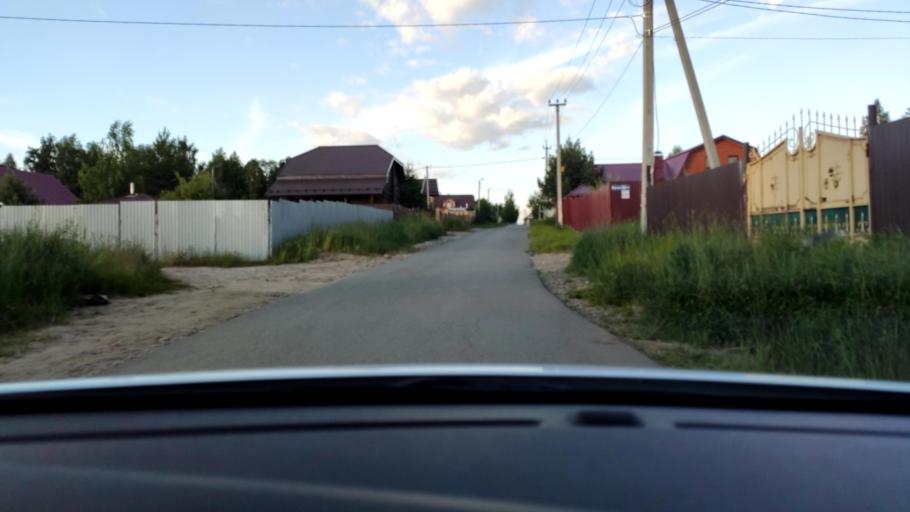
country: RU
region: Tatarstan
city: Stolbishchi
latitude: 55.7613
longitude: 49.2987
